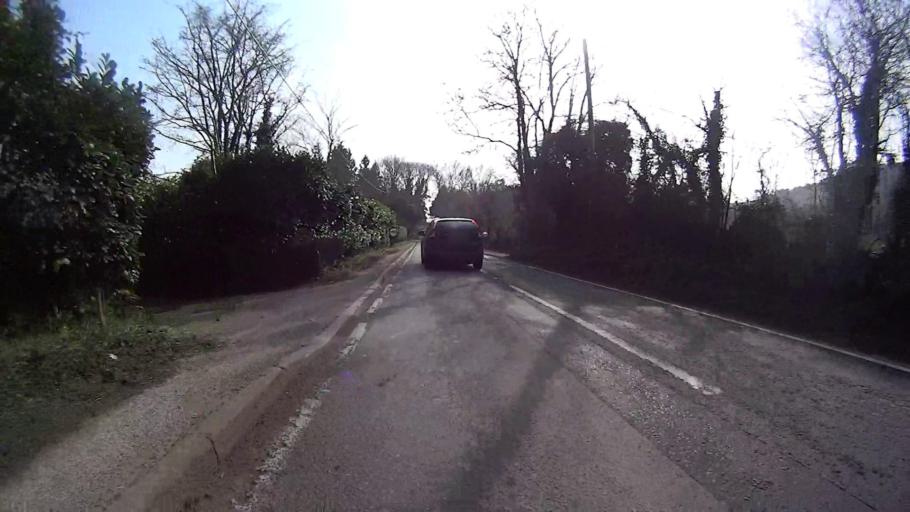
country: GB
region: England
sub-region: Surrey
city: Headley
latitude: 51.2563
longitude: -0.2619
